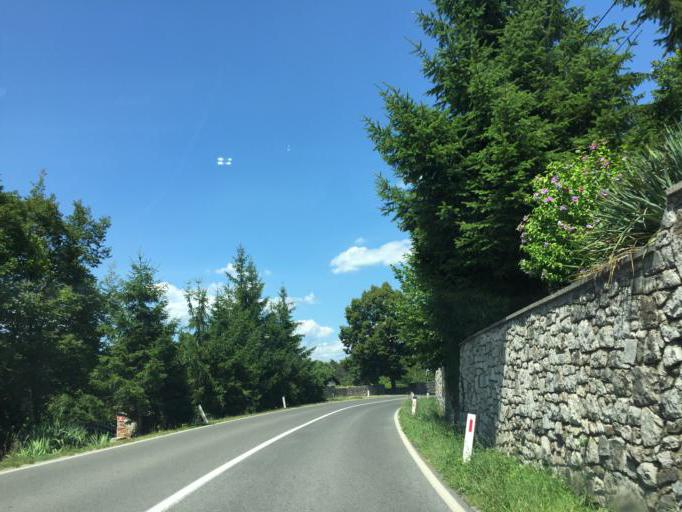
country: SI
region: Sezana
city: Sezana
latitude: 45.7259
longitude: 13.8669
